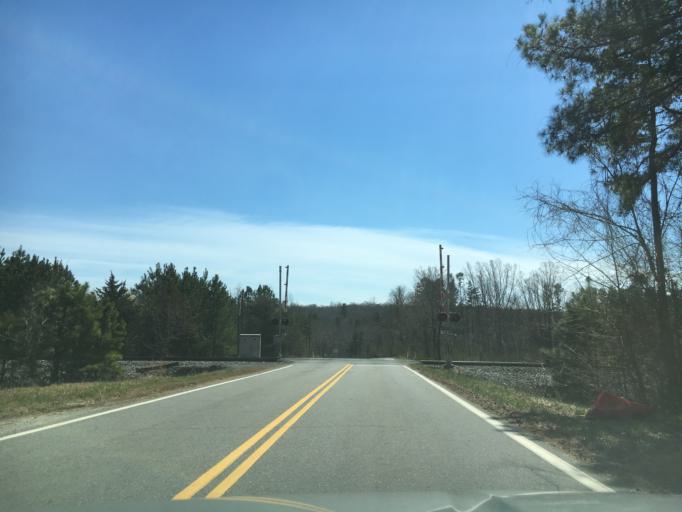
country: US
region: Virginia
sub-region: Halifax County
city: Halifax
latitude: 36.7660
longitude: -78.9164
